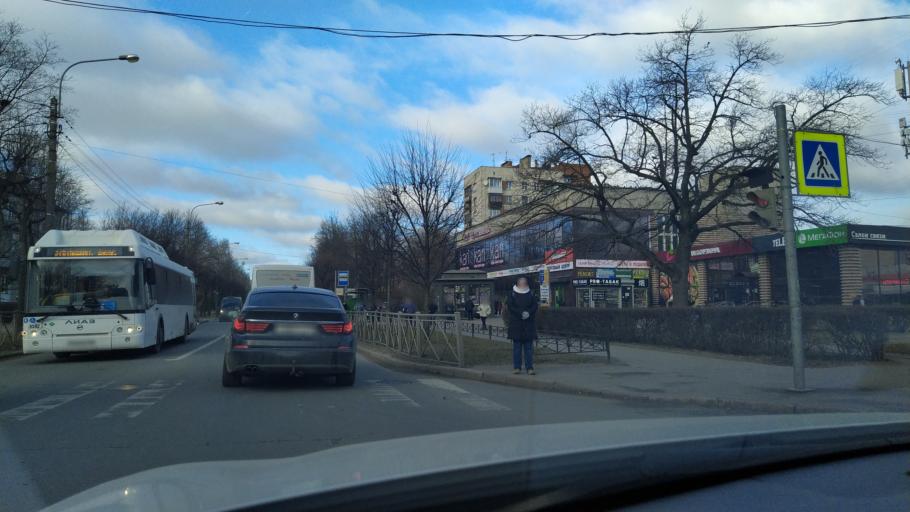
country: RU
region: St.-Petersburg
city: Pushkin
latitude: 59.7266
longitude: 30.4176
